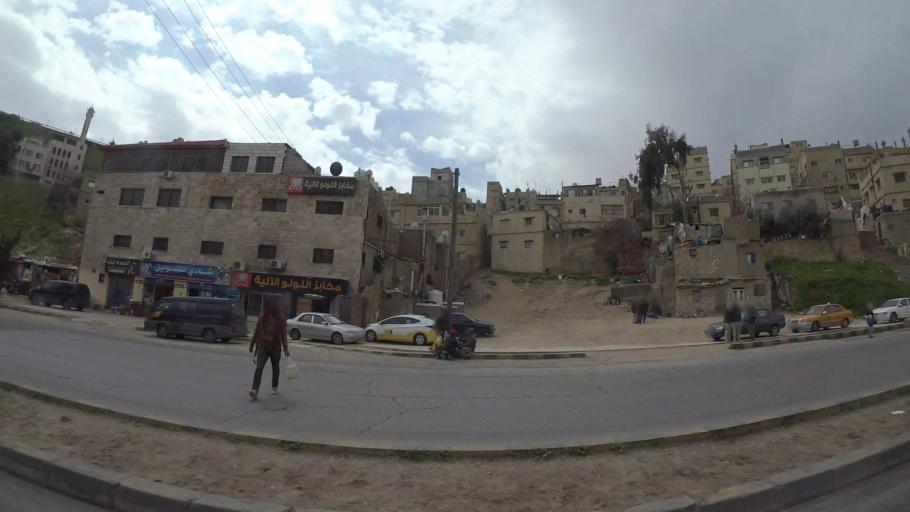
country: JO
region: Amman
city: Amman
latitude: 31.9565
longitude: 35.9375
